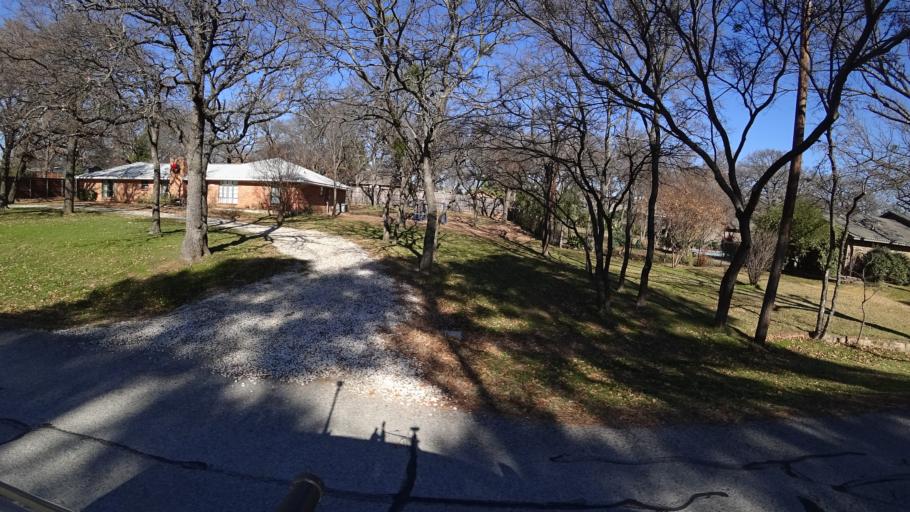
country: US
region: Texas
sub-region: Denton County
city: Lewisville
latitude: 33.0235
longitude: -97.0162
